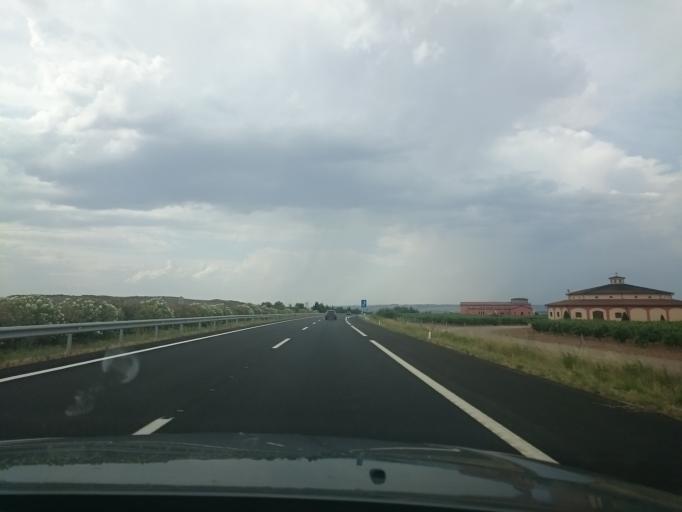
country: ES
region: La Rioja
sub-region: Provincia de La Rioja
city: Aldeanueva de Ebro
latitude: 42.2320
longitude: -1.9007
